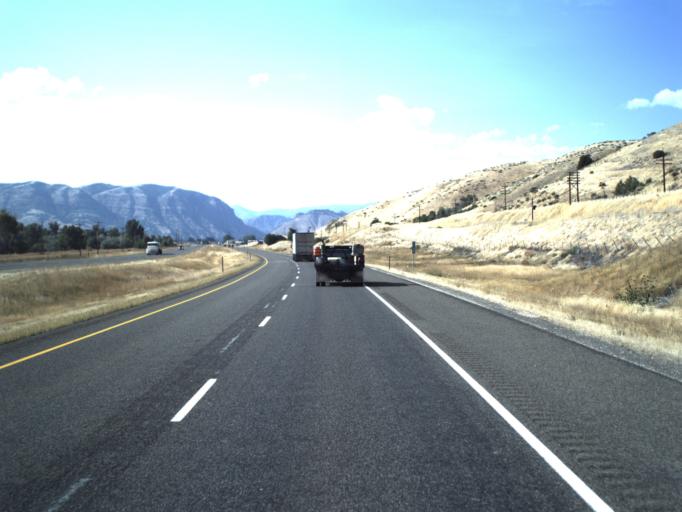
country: US
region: Utah
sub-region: Summit County
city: Coalville
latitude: 40.9994
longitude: -111.4671
